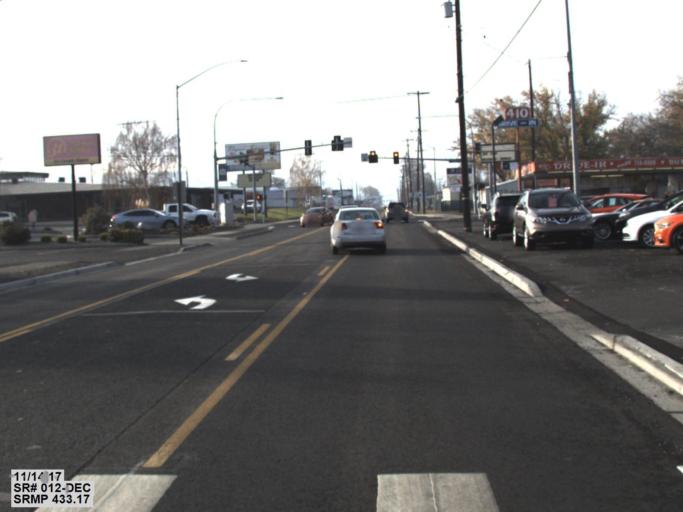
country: US
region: Washington
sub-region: Asotin County
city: Clarkston
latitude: 46.4199
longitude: -117.0576
